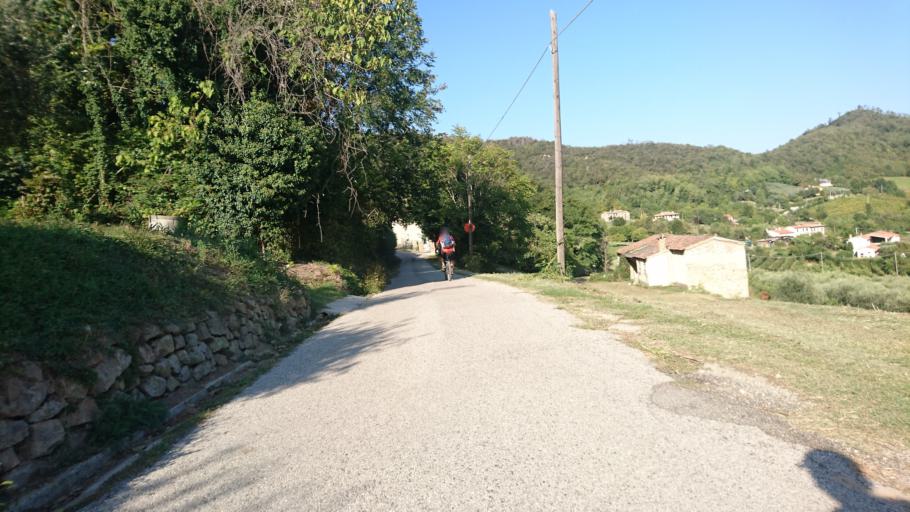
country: IT
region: Veneto
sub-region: Provincia di Padova
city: Galzignano
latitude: 45.3155
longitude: 11.7522
